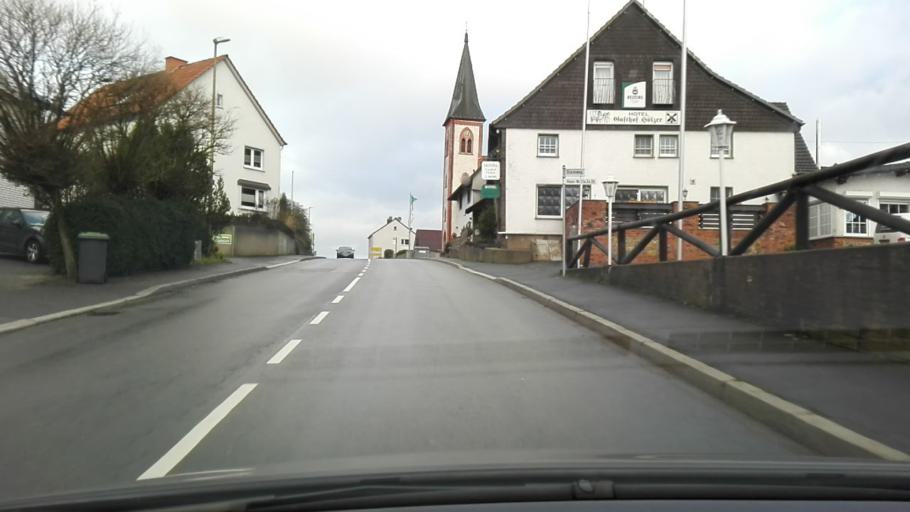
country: DE
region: North Rhine-Westphalia
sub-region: Regierungsbezirk Arnsberg
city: Frondenberg
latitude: 51.4889
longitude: 7.7824
